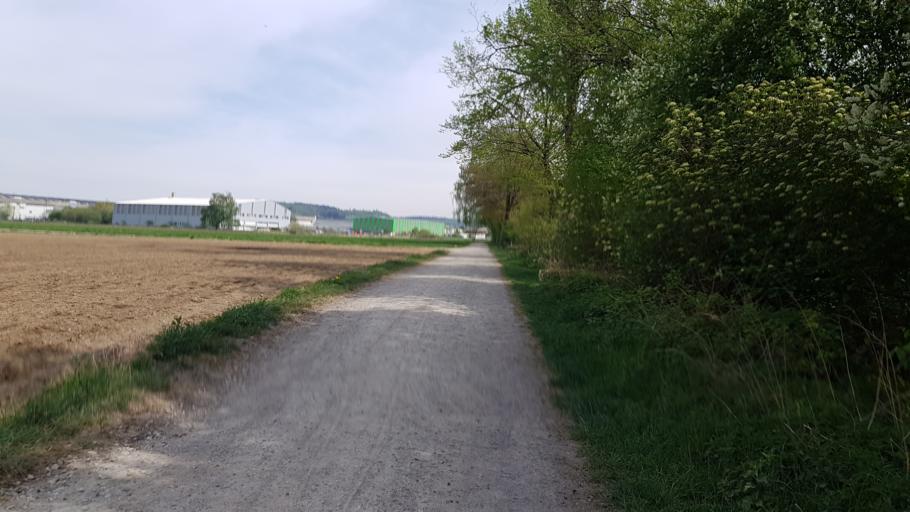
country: CH
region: Aargau
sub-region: Bezirk Kulm
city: Gontenschwil
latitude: 47.2680
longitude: 8.1665
